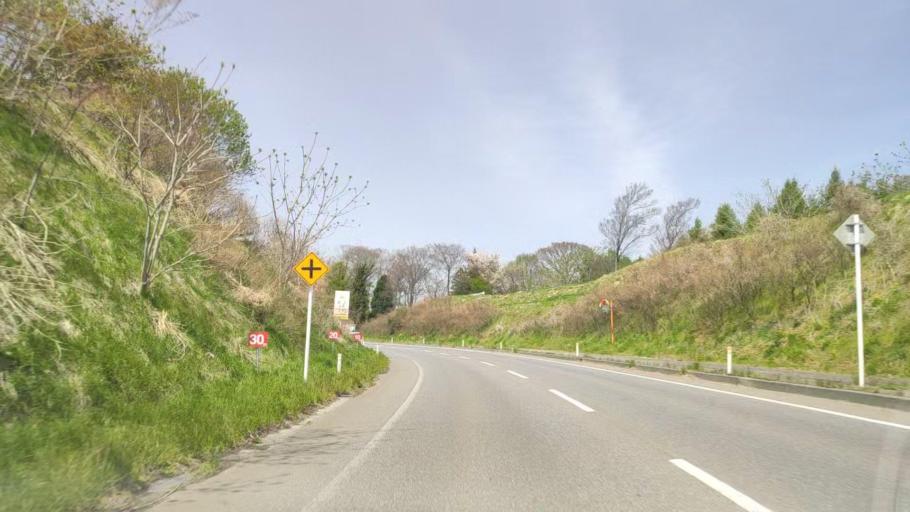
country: JP
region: Aomori
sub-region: Hachinohe Shi
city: Uchimaru
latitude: 40.5204
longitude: 141.4259
